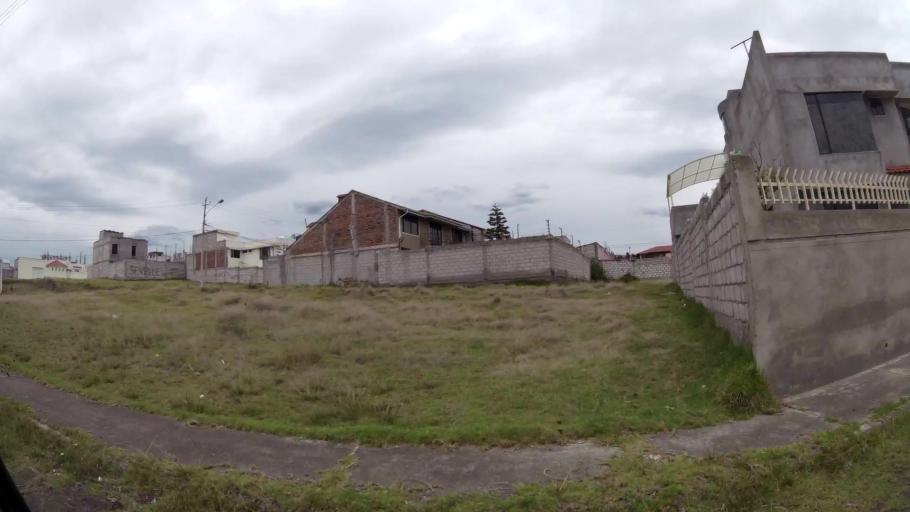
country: EC
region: Cotopaxi
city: Latacunga
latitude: -0.9694
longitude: -78.6135
